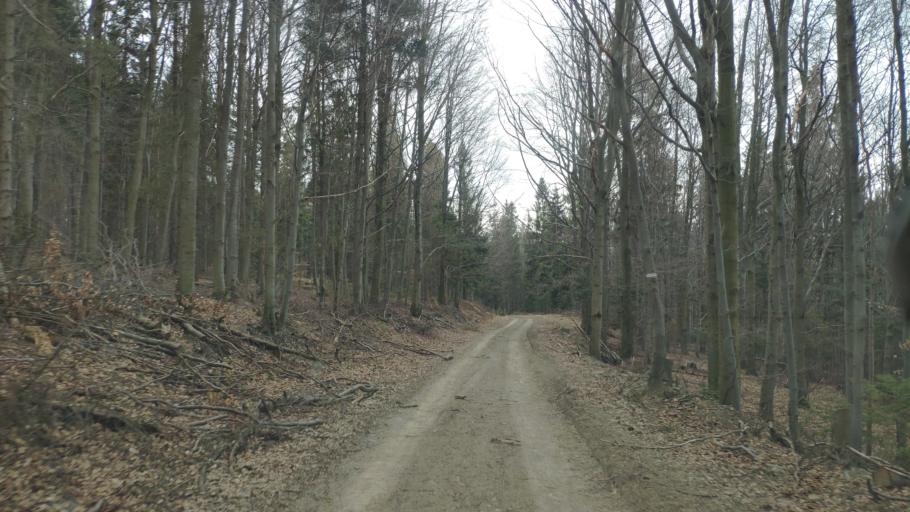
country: SK
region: Kosicky
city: Moldava nad Bodvou
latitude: 48.7538
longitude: 21.0410
